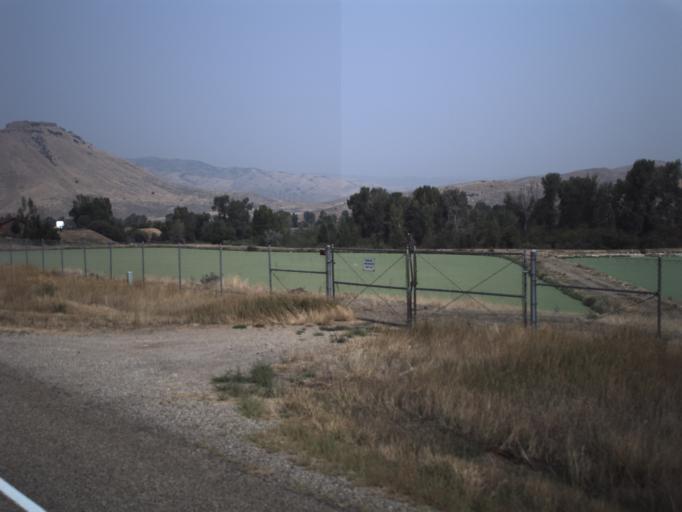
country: US
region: Utah
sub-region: Summit County
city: Coalville
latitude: 41.0302
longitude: -111.5104
